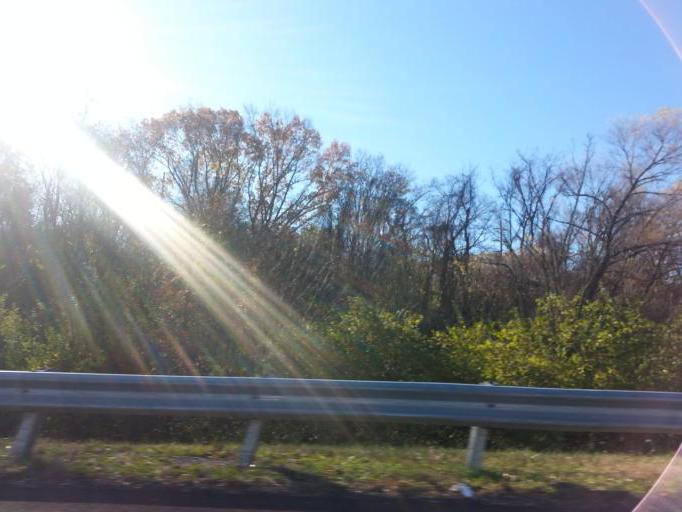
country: US
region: Tennessee
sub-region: Knox County
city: Knoxville
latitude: 35.9836
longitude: -83.9457
